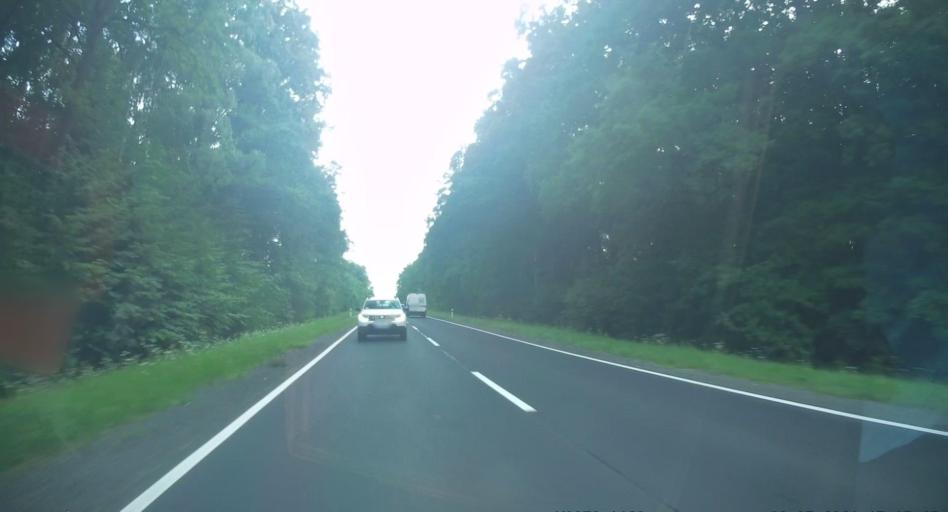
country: PL
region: Silesian Voivodeship
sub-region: Powiat czestochowski
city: Klomnice
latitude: 50.9519
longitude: 19.3993
